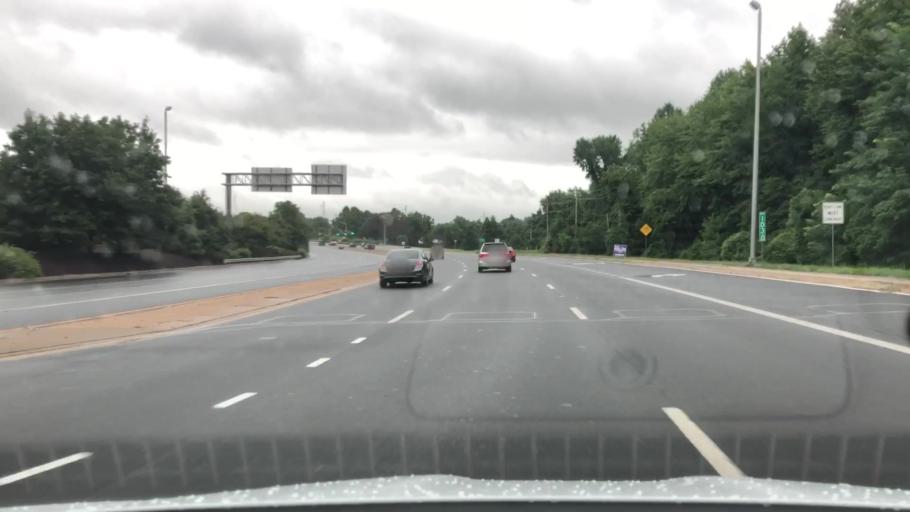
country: US
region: Delaware
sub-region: New Castle County
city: Newport
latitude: 39.6972
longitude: -75.6514
